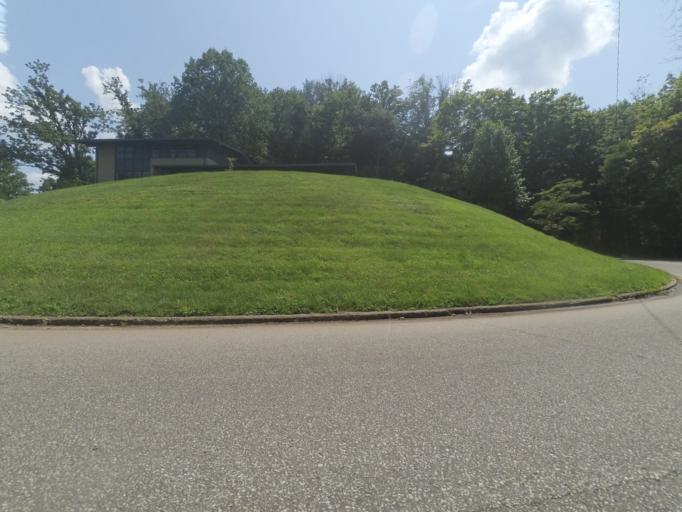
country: US
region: West Virginia
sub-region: Cabell County
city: Huntington
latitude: 38.4028
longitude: -82.4307
